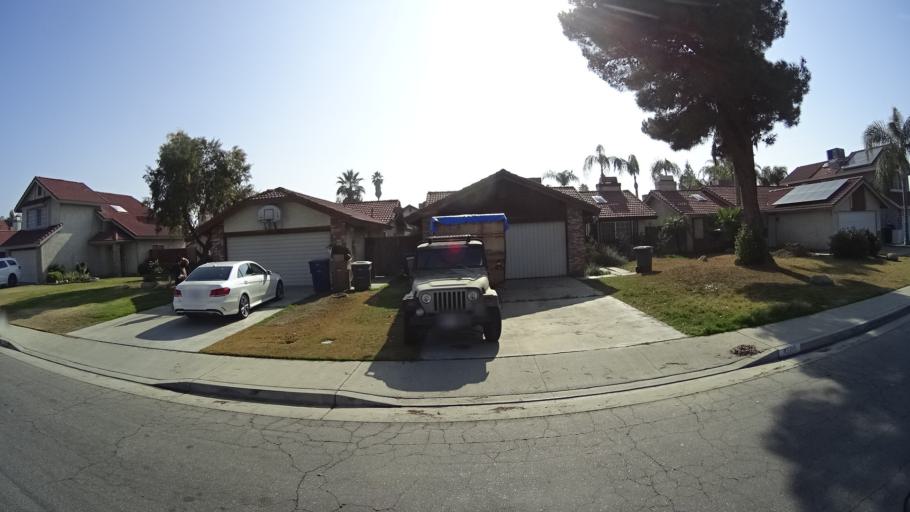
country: US
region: California
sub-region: Kern County
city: Bakersfield
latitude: 35.3206
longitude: -119.0528
